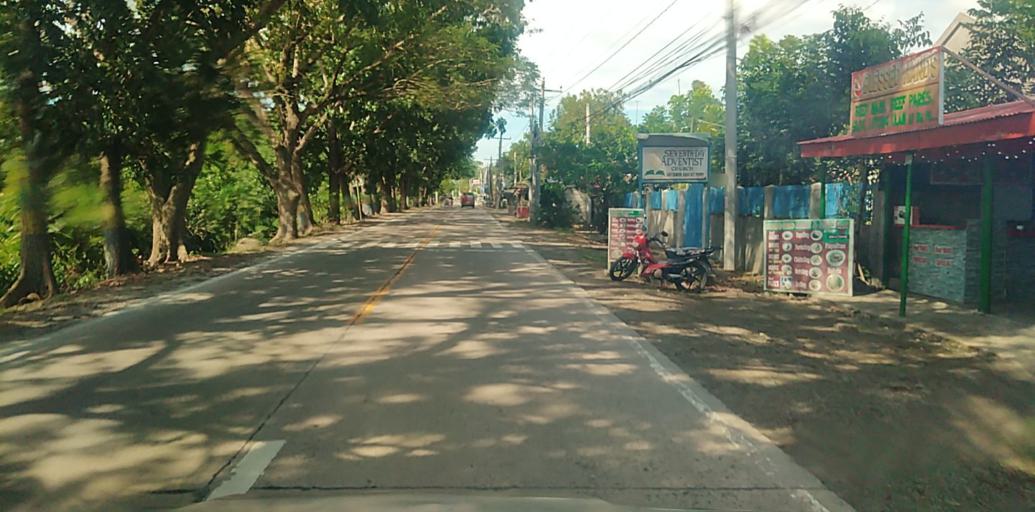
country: PH
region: Central Luzon
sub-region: Province of Pampanga
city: Arayat
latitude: 15.1510
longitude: 120.7446
